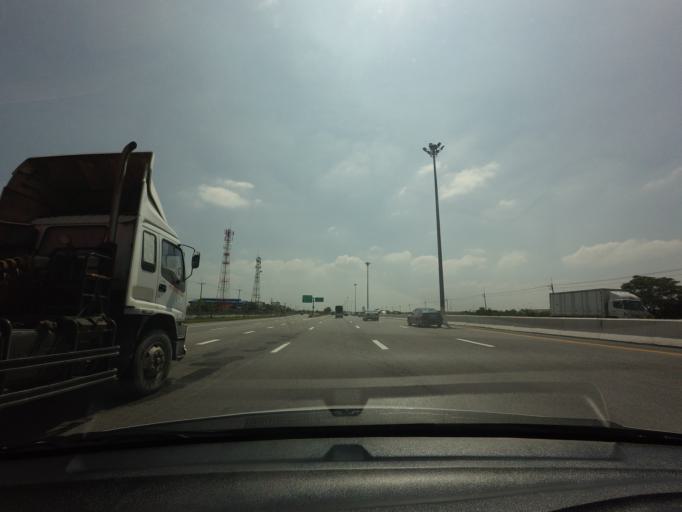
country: TH
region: Chachoengsao
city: Bang Pakong
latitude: 13.6058
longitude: 100.9440
